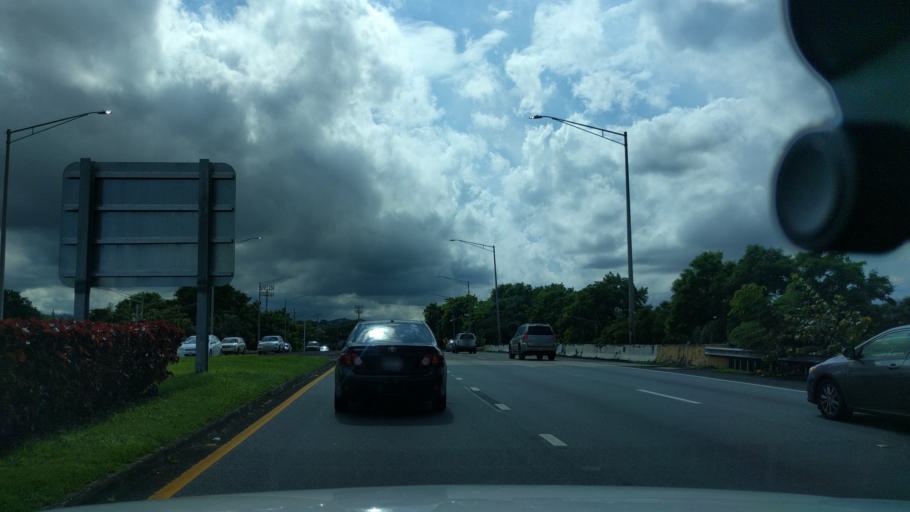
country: PR
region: Bayamon
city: Bayamon
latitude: 18.3698
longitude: -66.1660
